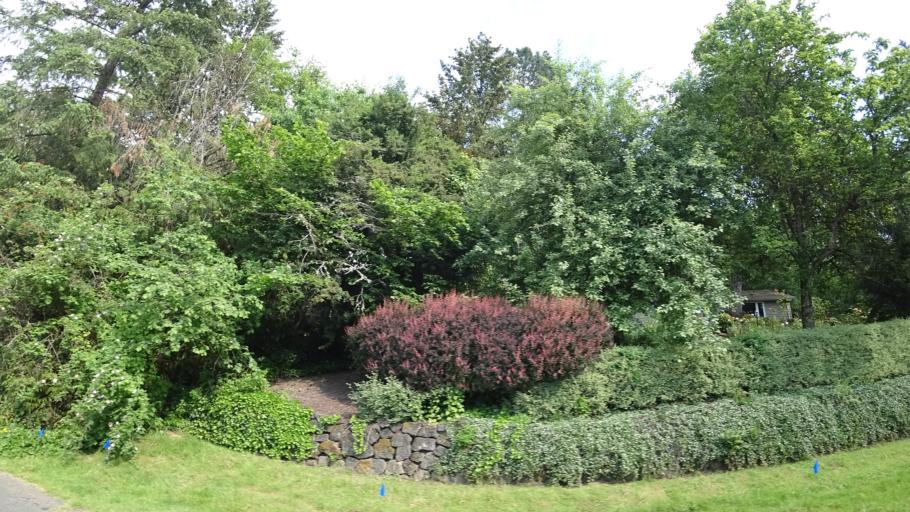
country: US
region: Oregon
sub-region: Washington County
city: Garden Home-Whitford
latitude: 45.4578
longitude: -122.7415
